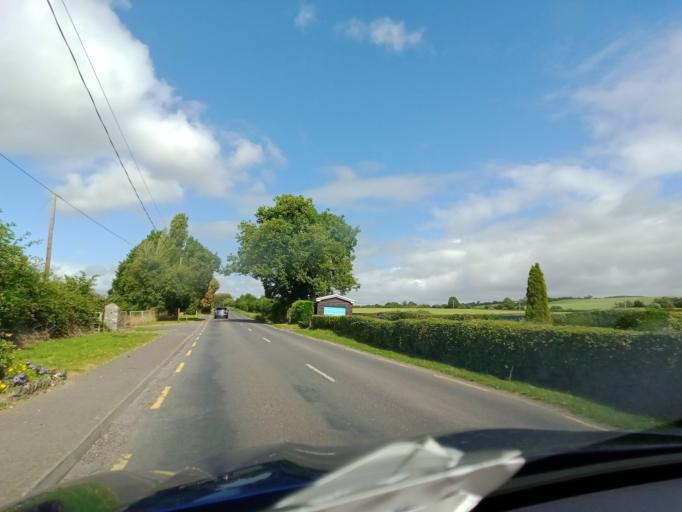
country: IE
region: Leinster
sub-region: Laois
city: Abbeyleix
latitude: 52.9527
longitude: -7.3027
